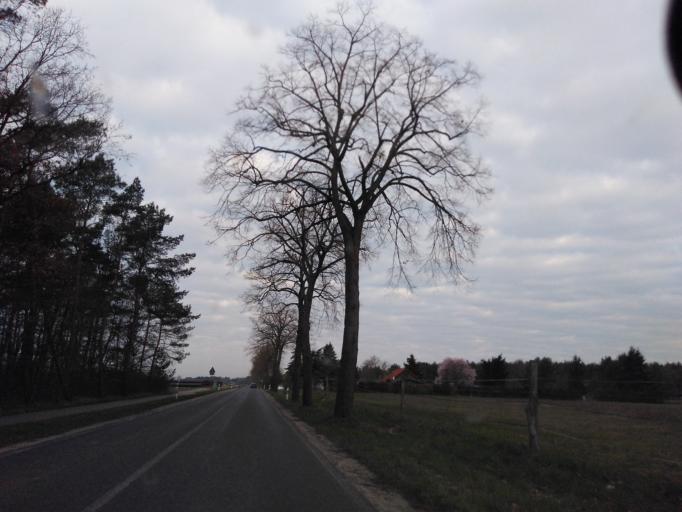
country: DE
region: Brandenburg
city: Strausberg
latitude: 52.5678
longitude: 13.9236
